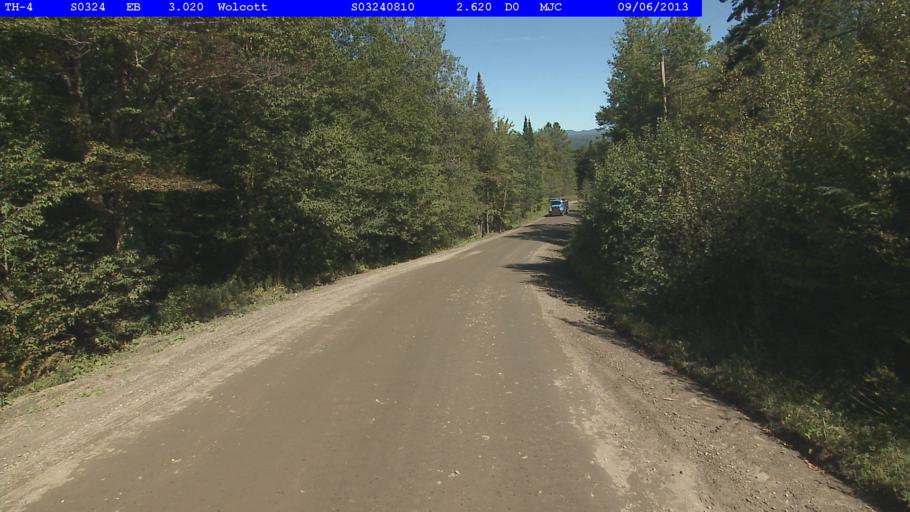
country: US
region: Vermont
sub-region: Lamoille County
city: Morrisville
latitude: 44.5447
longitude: -72.4850
